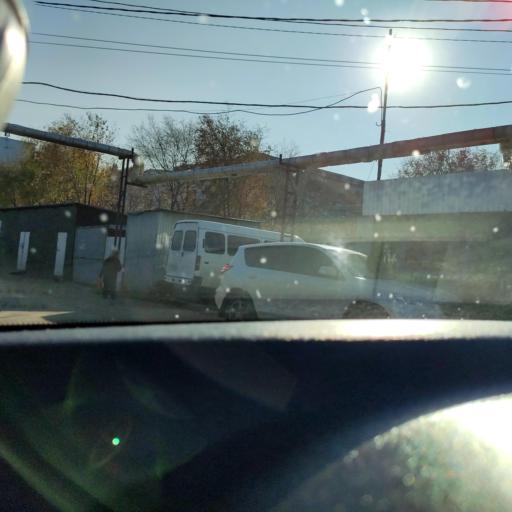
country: RU
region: Samara
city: Samara
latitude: 53.2105
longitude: 50.2709
